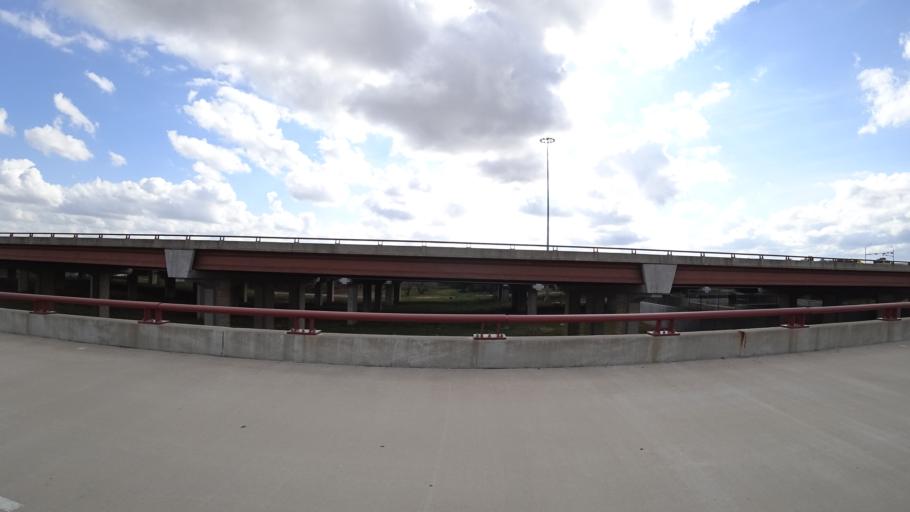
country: US
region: Texas
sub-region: Williamson County
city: Brushy Creek
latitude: 30.4804
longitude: -97.7159
